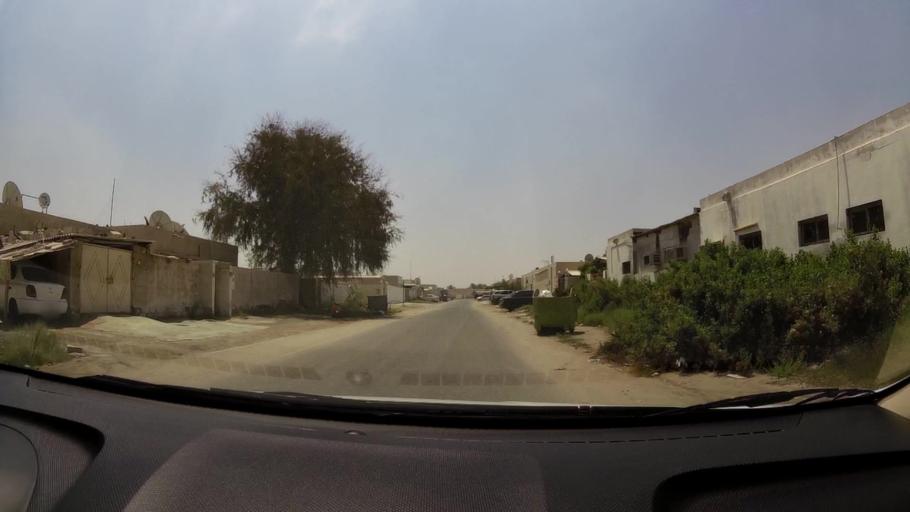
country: AE
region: Umm al Qaywayn
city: Umm al Qaywayn
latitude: 25.5595
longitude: 55.5555
